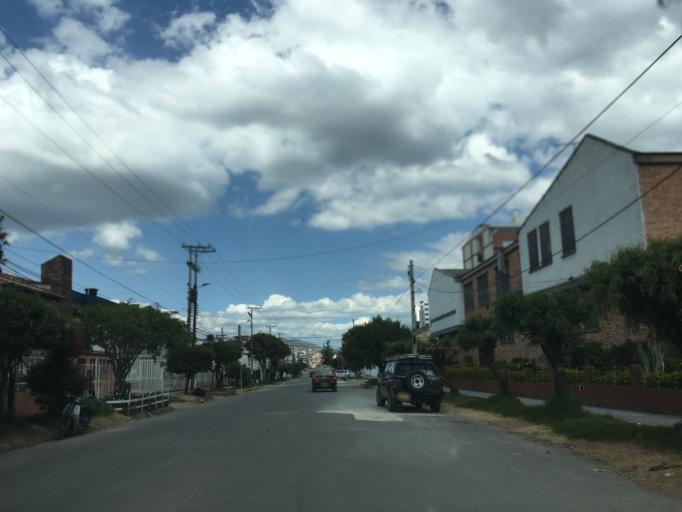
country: CO
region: Boyaca
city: Sogamoso
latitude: 5.7188
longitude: -72.9230
